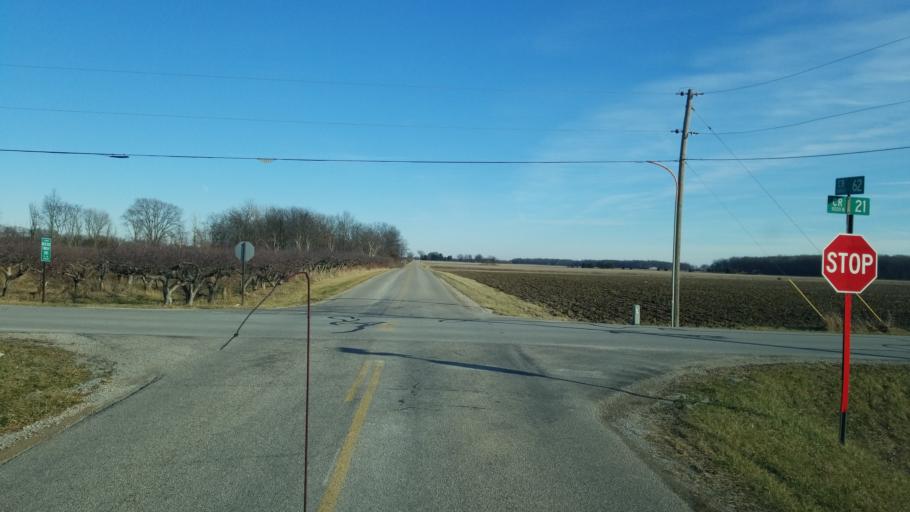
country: US
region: Ohio
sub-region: Sandusky County
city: Mount Carmel
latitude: 41.2561
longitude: -82.9755
